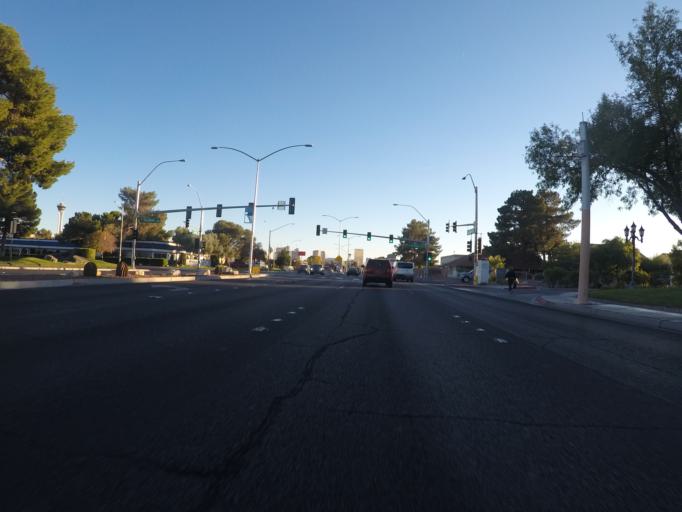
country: US
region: Nevada
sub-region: Clark County
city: Las Vegas
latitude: 36.1630
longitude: -115.1728
